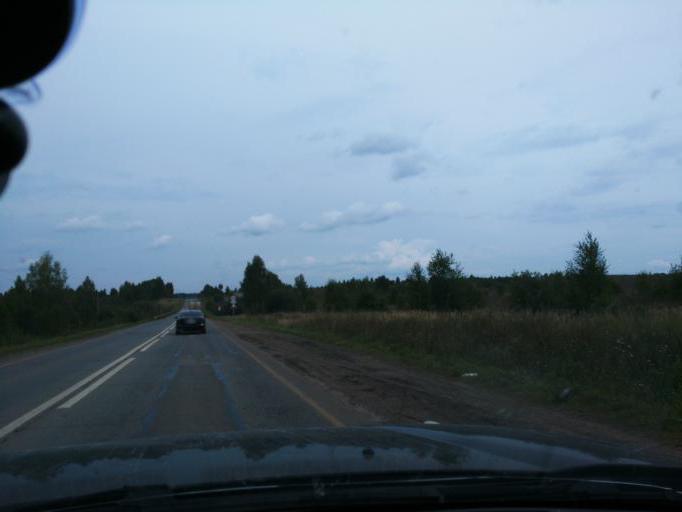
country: RU
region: Bashkortostan
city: Verkhniye Tatyshly
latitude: 56.4854
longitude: 55.8000
